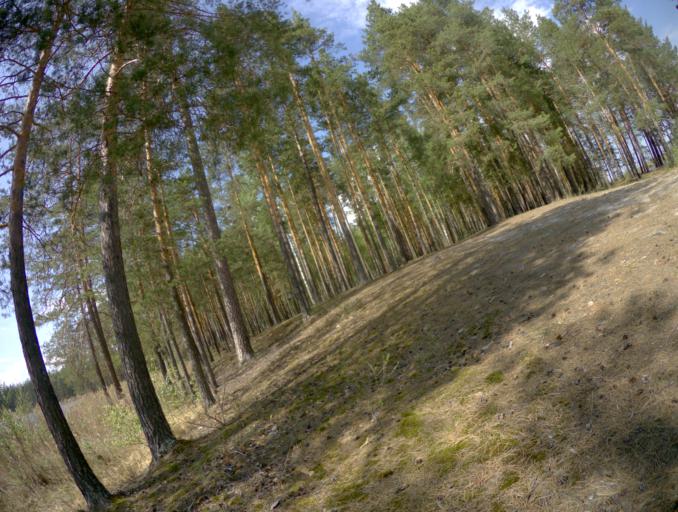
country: RU
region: Ivanovo
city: Talitsy
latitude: 56.4745
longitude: 42.1896
